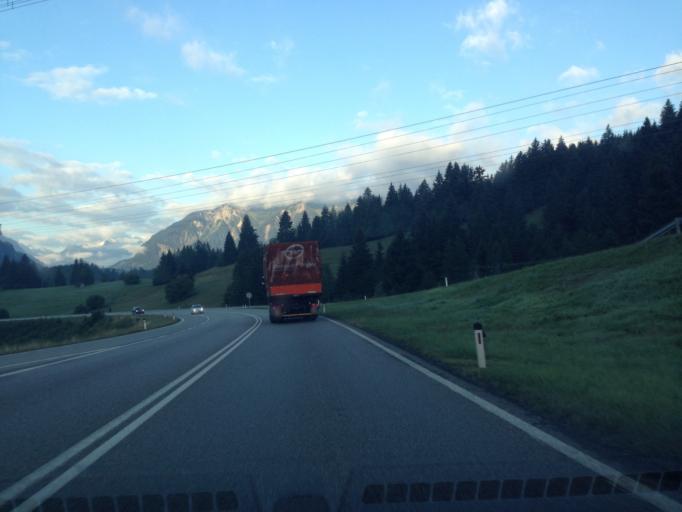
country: AT
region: Tyrol
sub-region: Politischer Bezirk Reutte
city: Breitenwang
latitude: 47.4897
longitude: 10.7464
